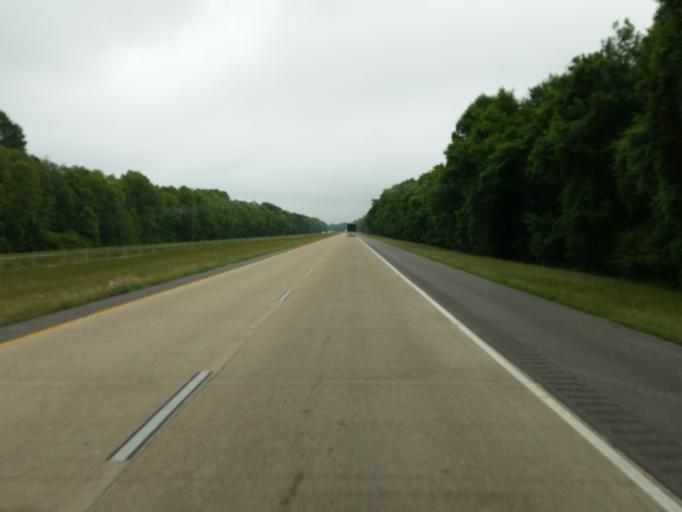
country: US
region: Louisiana
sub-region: Madison Parish
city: Tallulah
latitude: 32.3446
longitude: -91.0791
